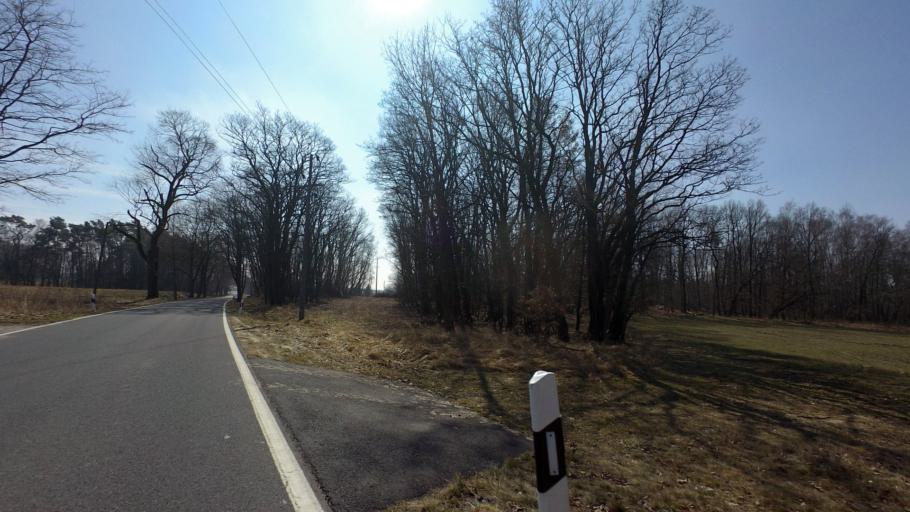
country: DE
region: Brandenburg
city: Wiesenburg
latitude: 52.0253
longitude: 12.5289
